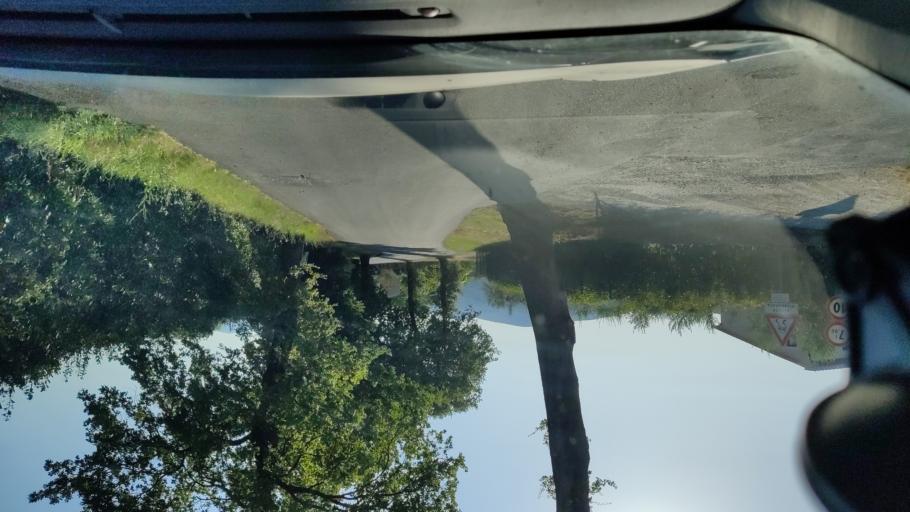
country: IT
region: Umbria
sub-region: Provincia di Terni
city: Amelia
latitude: 42.5401
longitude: 12.4031
